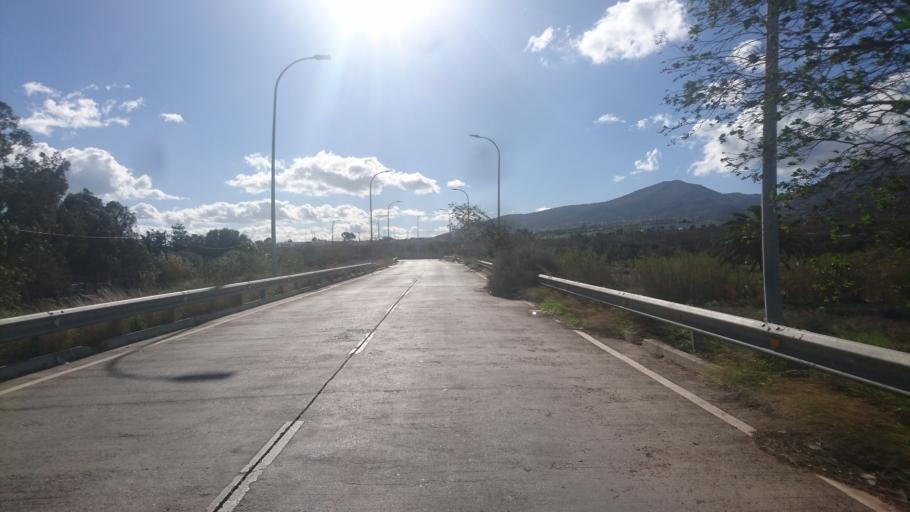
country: ES
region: Melilla
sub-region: Melilla
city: Melilla
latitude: 35.2688
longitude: -2.9404
